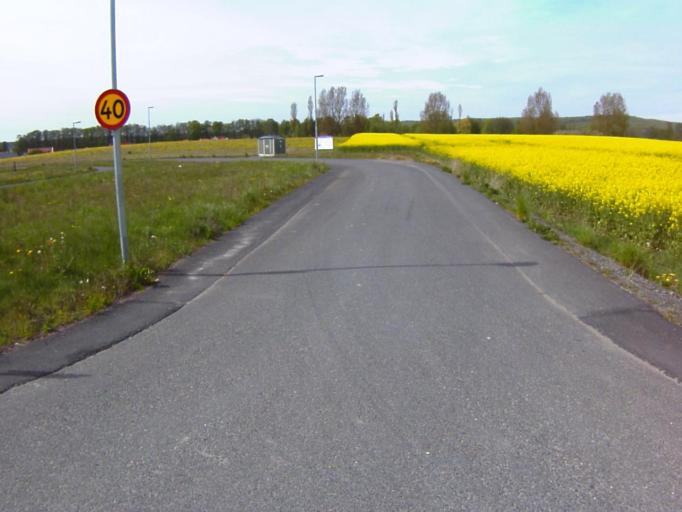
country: SE
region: Skane
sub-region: Kristianstads Kommun
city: Fjalkinge
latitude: 56.0777
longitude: 14.2212
